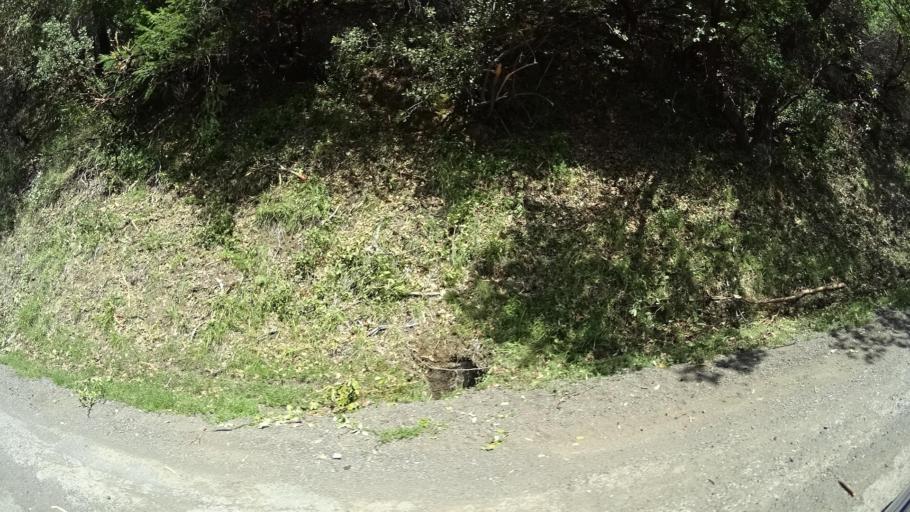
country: US
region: California
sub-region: Humboldt County
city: Redway
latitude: 40.2293
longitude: -123.6459
